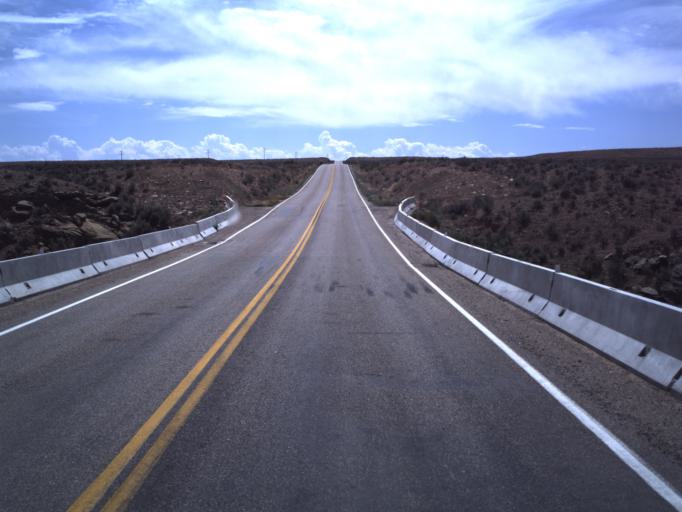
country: US
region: Utah
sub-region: Uintah County
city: Maeser
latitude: 40.3067
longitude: -109.6900
